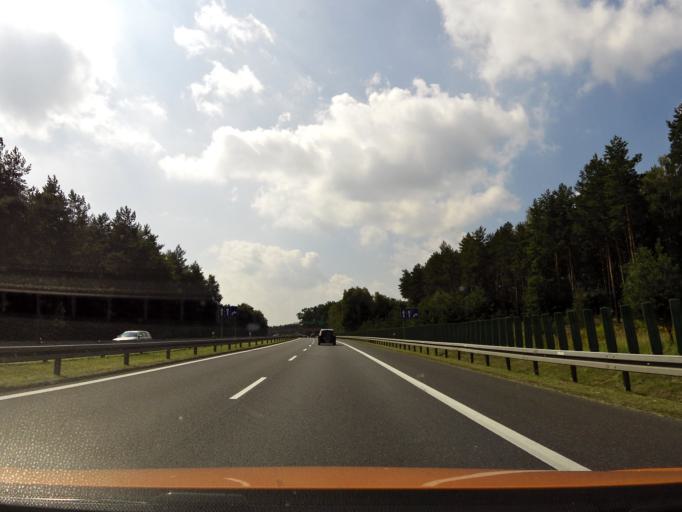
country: PL
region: West Pomeranian Voivodeship
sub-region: Powiat goleniowski
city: Goleniow
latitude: 53.5738
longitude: 14.8018
